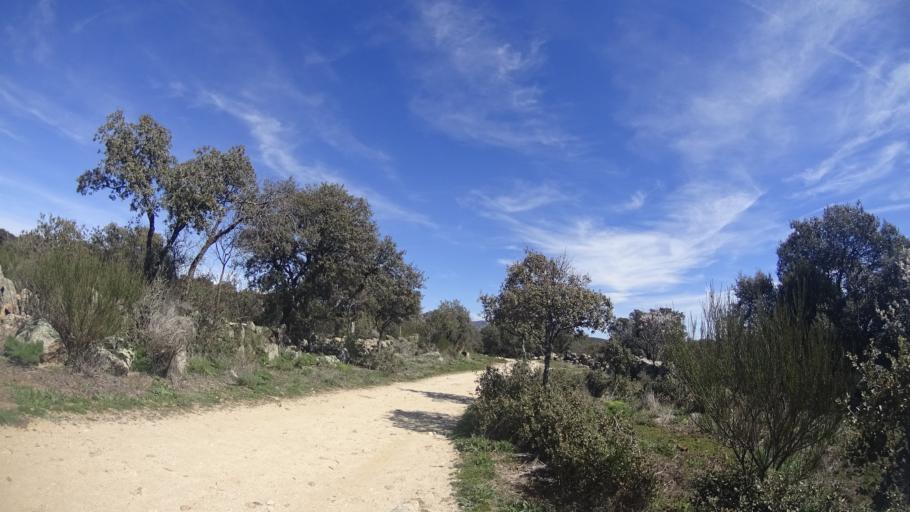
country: ES
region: Madrid
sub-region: Provincia de Madrid
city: Galapagar
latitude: 40.5863
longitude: -3.9862
